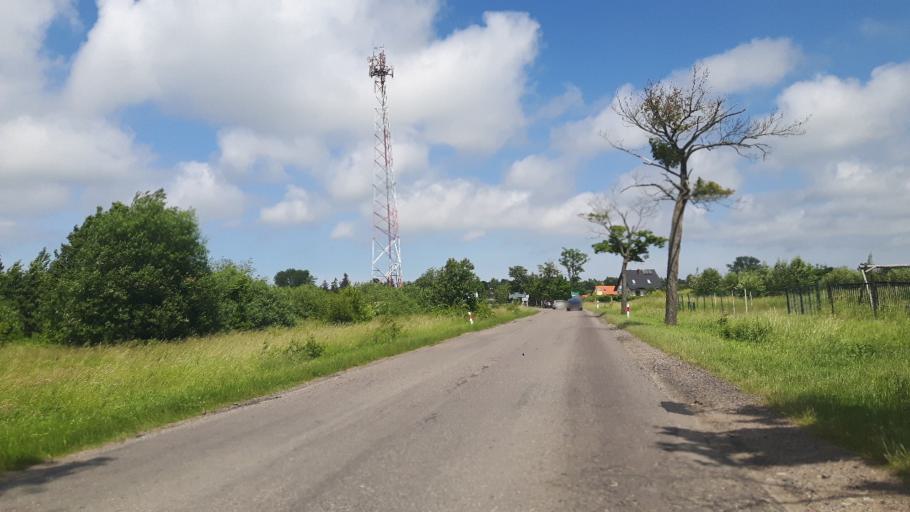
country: PL
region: Pomeranian Voivodeship
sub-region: Powiat slupski
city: Ustka
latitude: 54.5342
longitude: 16.8198
